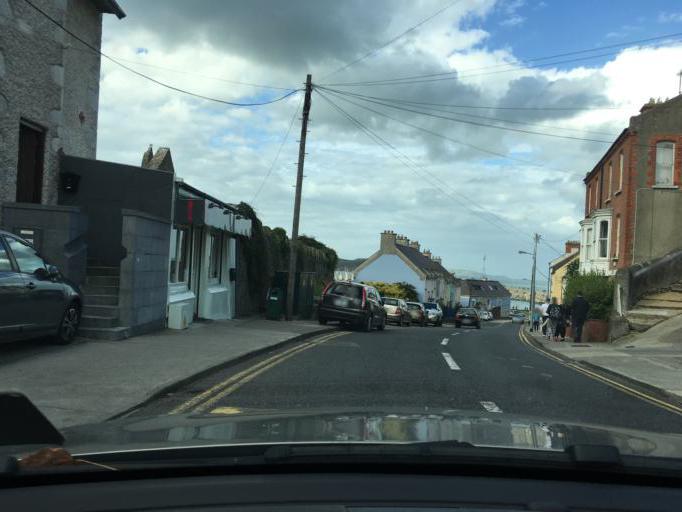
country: IE
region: Leinster
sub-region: Fingal County
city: Howth
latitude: 53.3871
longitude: -6.0656
